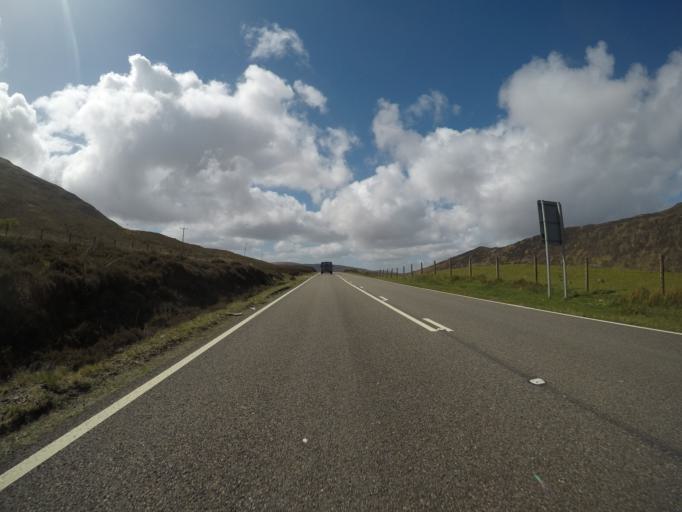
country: GB
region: Scotland
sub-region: Highland
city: Portree
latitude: 57.3032
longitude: -6.1389
